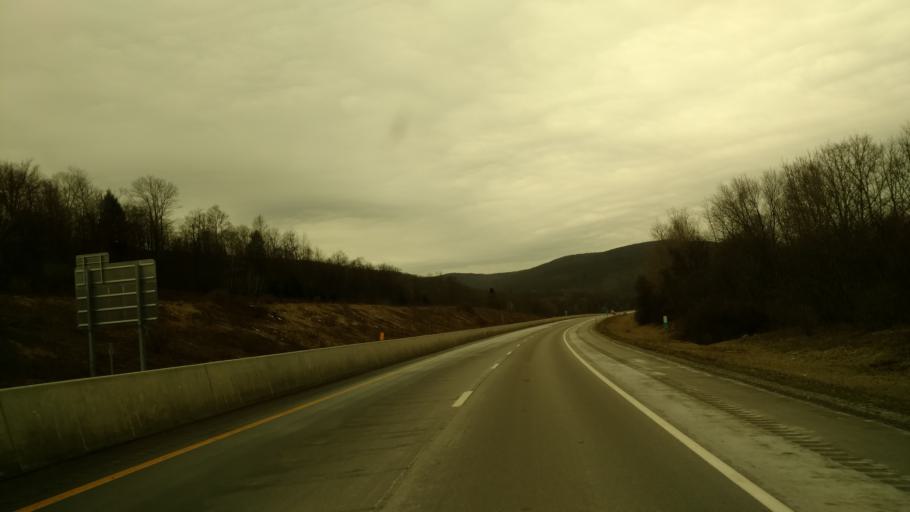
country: US
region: New York
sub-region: Cattaraugus County
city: Salamanca
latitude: 42.0940
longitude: -78.6533
